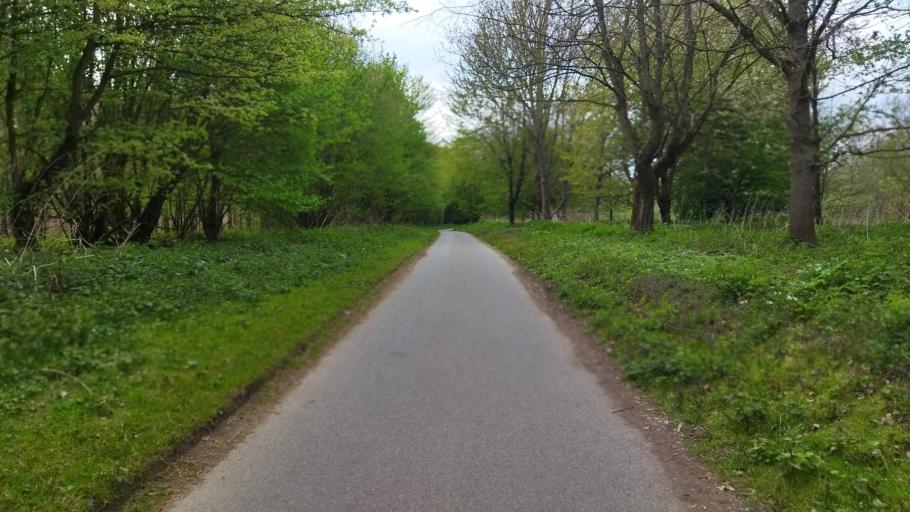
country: DE
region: North Rhine-Westphalia
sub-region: Regierungsbezirk Dusseldorf
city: Essen
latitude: 51.4220
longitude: 7.0625
